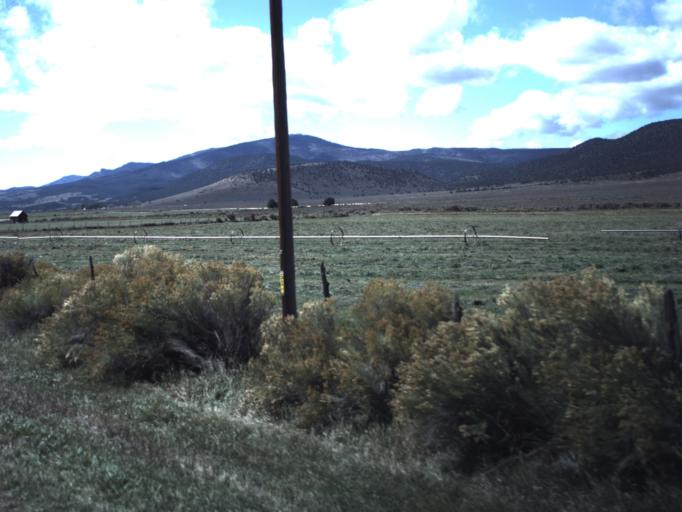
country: US
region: Utah
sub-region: Sevier County
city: Monroe
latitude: 38.4584
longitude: -111.9106
